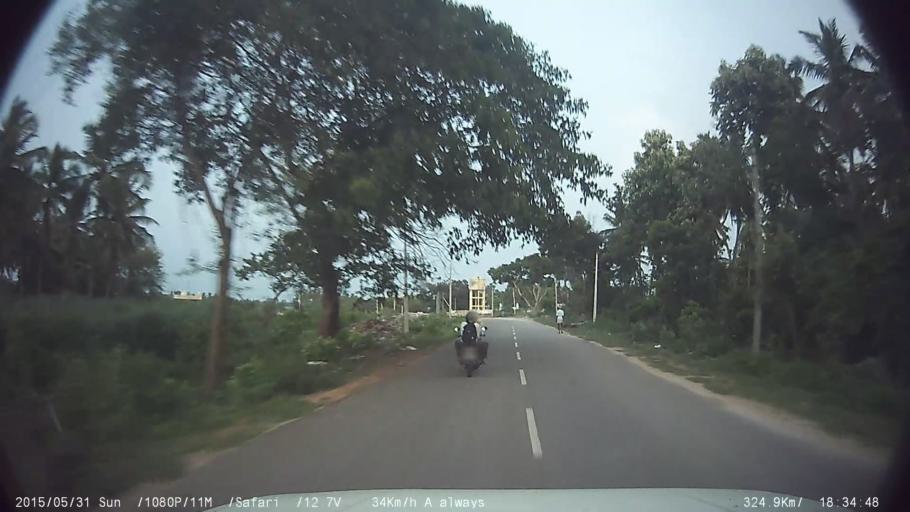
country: IN
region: Karnataka
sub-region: Mysore
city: Nanjangud
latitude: 12.1449
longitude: 76.7581
